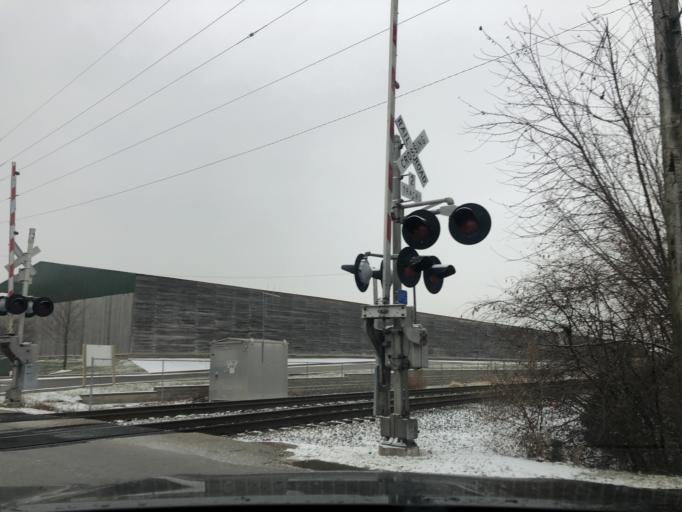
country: US
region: Illinois
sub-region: Cook County
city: Evergreen Park
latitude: 41.7282
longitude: -87.6874
